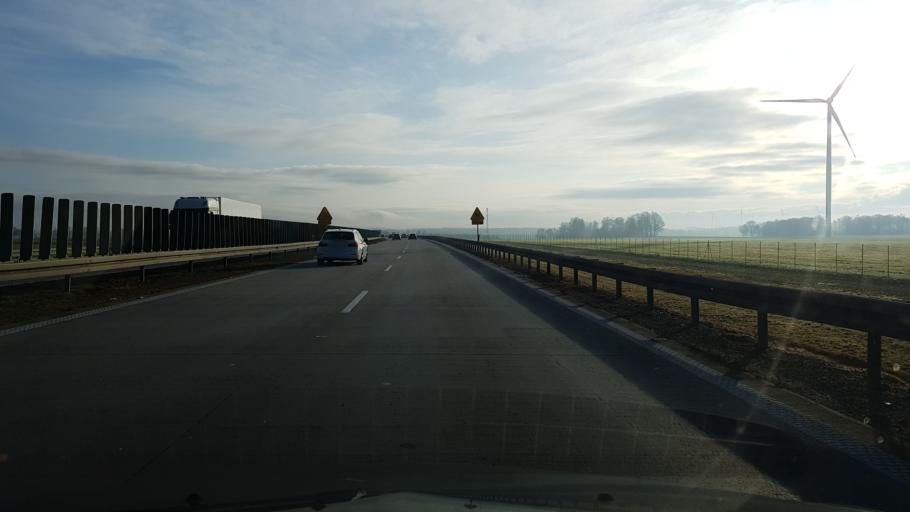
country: PL
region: Lower Silesian Voivodeship
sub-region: Powiat zlotoryjski
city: Olszanica
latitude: 51.2578
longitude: 15.8342
